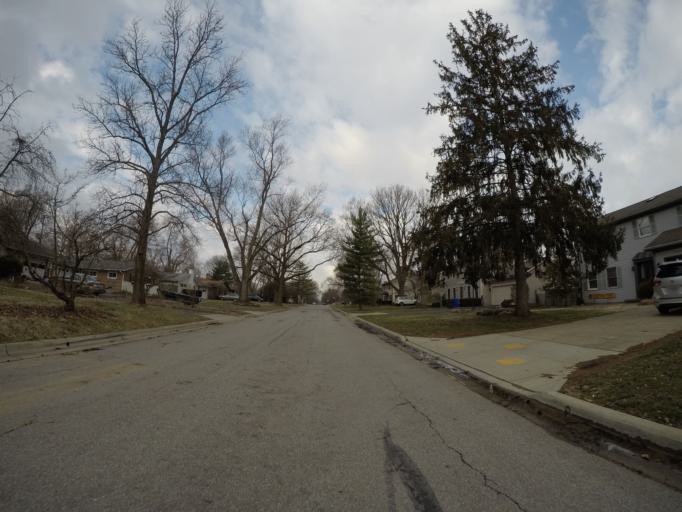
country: US
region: Ohio
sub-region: Franklin County
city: Upper Arlington
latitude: 40.0288
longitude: -83.0792
